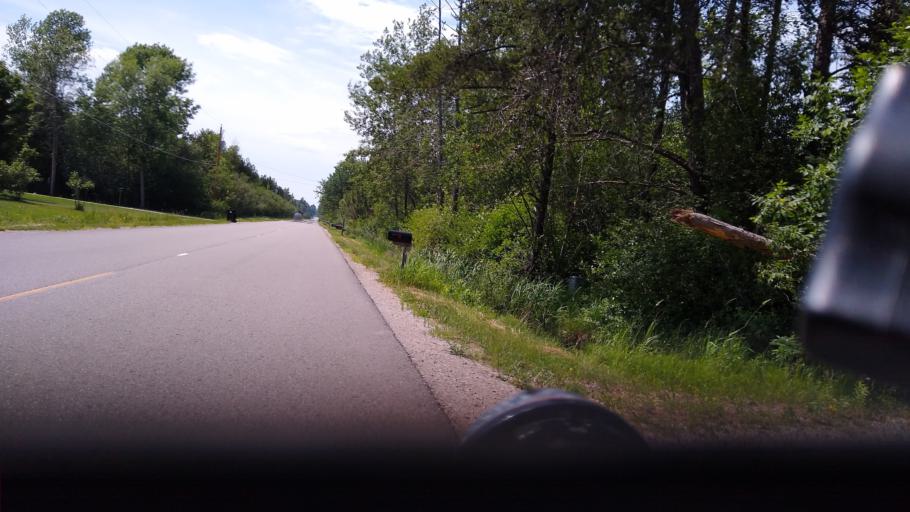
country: US
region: Michigan
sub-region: Delta County
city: Escanaba
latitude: 45.7099
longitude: -87.1037
